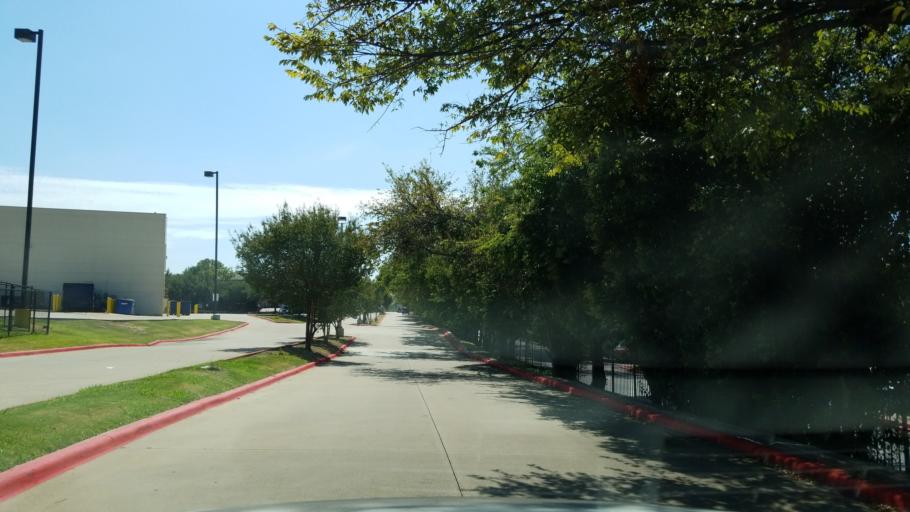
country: US
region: Texas
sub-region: Dallas County
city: Addison
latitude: 32.9533
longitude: -96.8065
